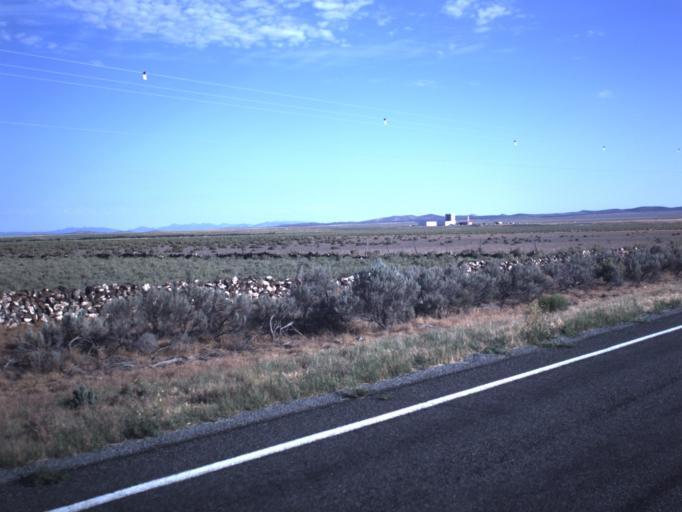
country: US
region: Utah
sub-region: Iron County
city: Enoch
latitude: 37.8612
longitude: -113.0316
